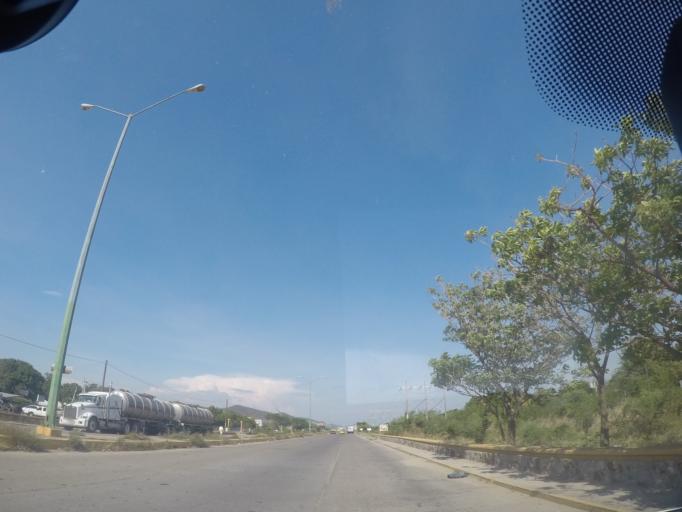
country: MX
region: Oaxaca
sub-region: Salina Cruz
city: Salina Cruz
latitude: 16.2206
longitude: -95.1986
